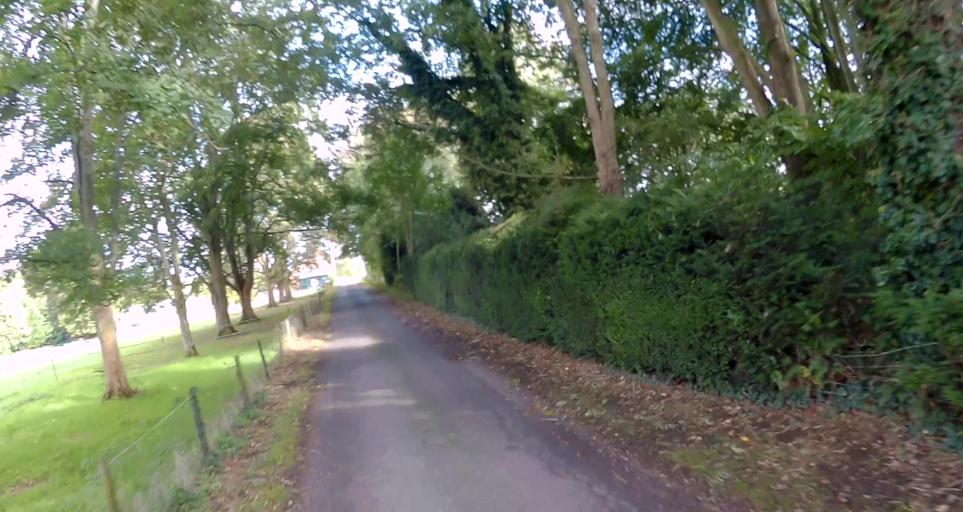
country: GB
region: England
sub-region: Hampshire
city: Kings Worthy
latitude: 51.0912
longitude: -1.2269
